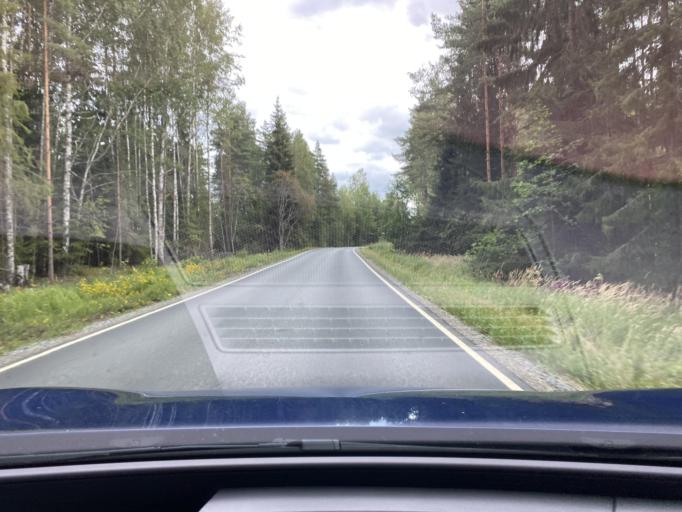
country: FI
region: Pirkanmaa
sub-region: Lounais-Pirkanmaa
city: Vammala
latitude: 61.3011
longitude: 22.9621
